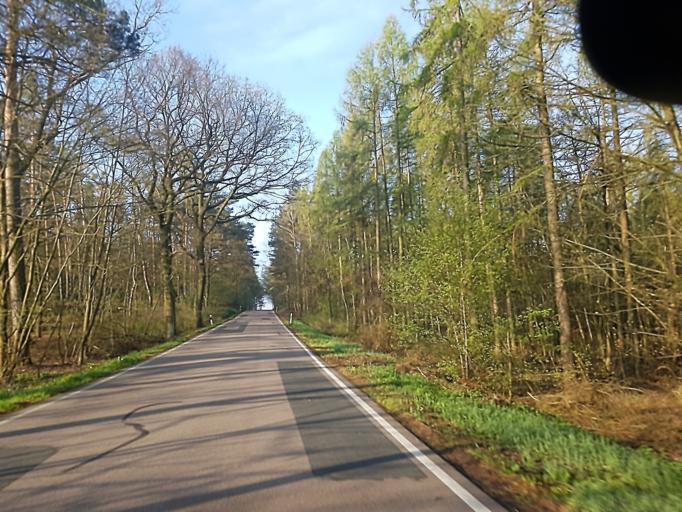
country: DE
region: Saxony
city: Cavertitz
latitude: 51.4189
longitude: 13.1493
